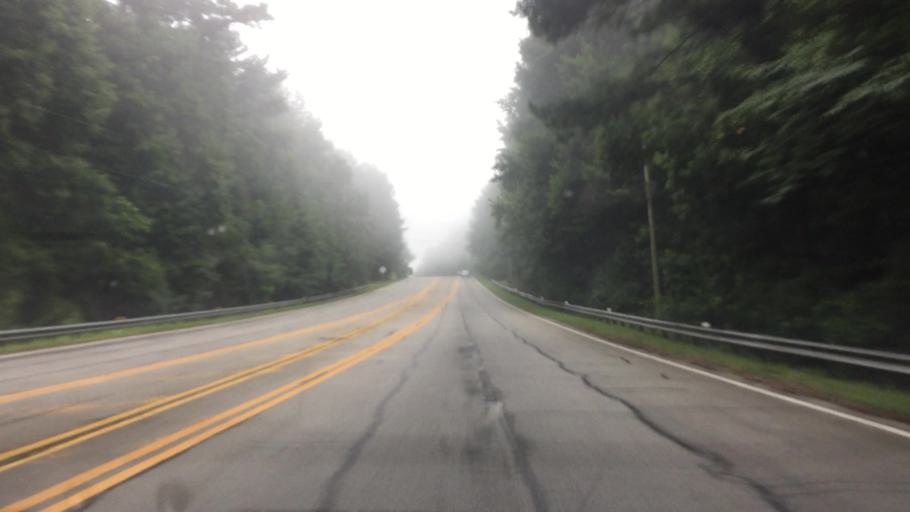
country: US
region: Georgia
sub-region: DeKalb County
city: Pine Mountain
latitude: 33.6398
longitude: -84.1850
